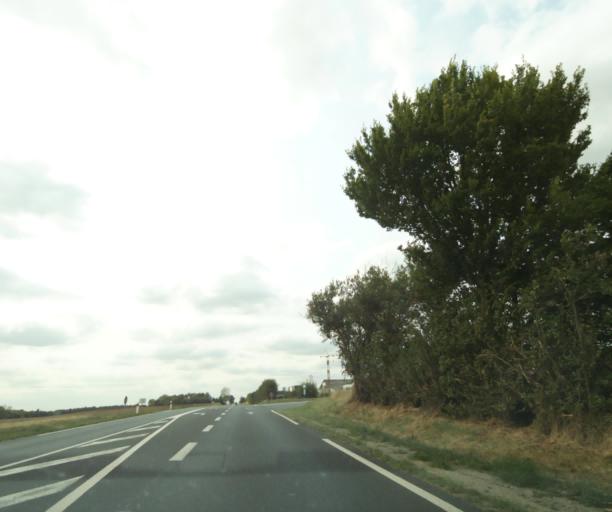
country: FR
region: Centre
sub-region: Departement de l'Indre
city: Buzancais
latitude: 46.9048
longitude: 1.3553
